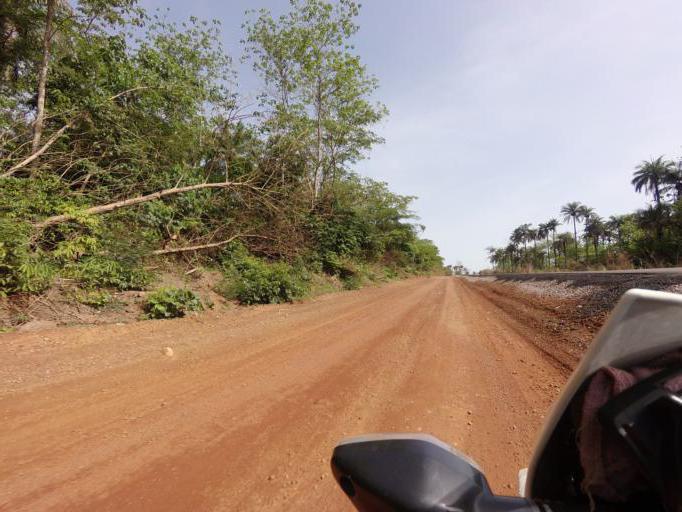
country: SL
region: Northern Province
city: Makeni
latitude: 9.0402
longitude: -12.1717
